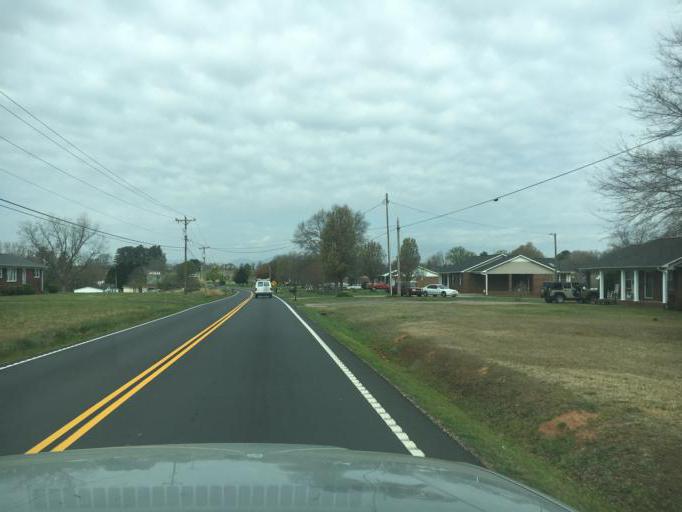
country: US
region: South Carolina
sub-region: Spartanburg County
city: Inman Mills
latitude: 35.0563
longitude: -82.1467
